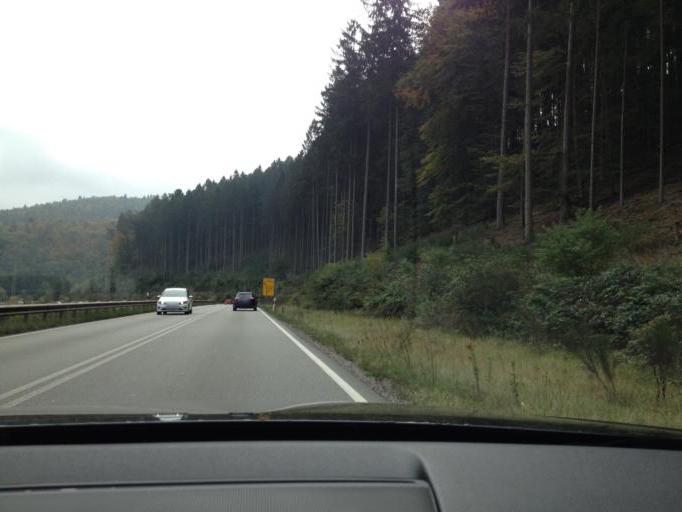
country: DE
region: Rheinland-Pfalz
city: Hinterweidenthal
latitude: 49.1967
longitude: 7.7341
